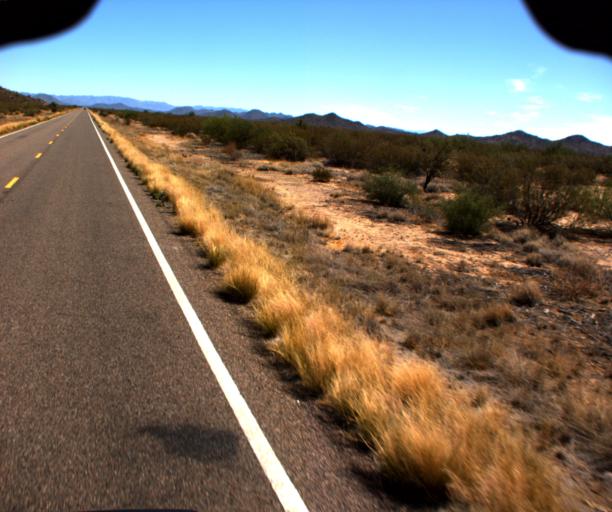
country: US
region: Arizona
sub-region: Yavapai County
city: Congress
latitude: 34.0029
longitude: -113.1181
